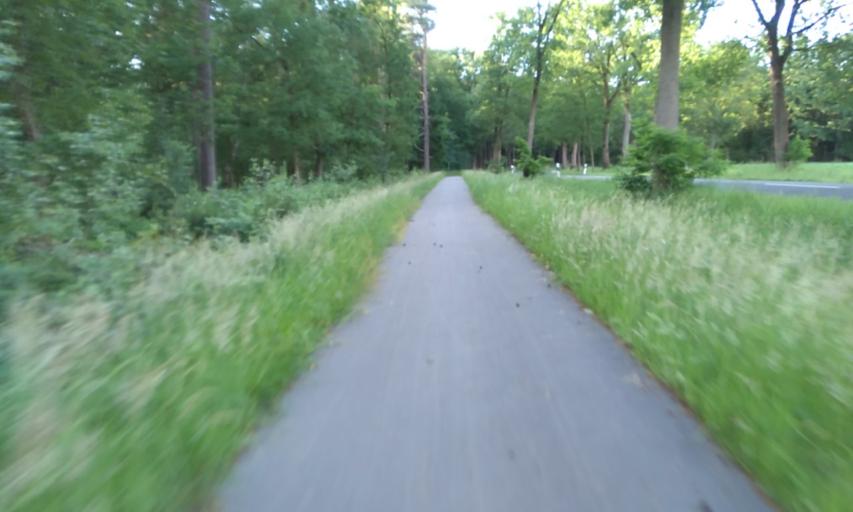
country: DE
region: Lower Saxony
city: Anderlingen
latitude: 53.3613
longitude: 9.3043
